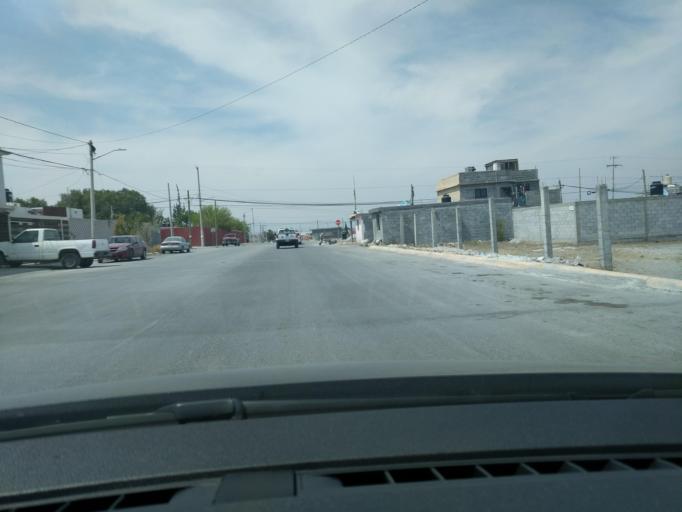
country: MX
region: Coahuila
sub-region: Arteaga
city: Arteaga
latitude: 25.4285
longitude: -100.9072
